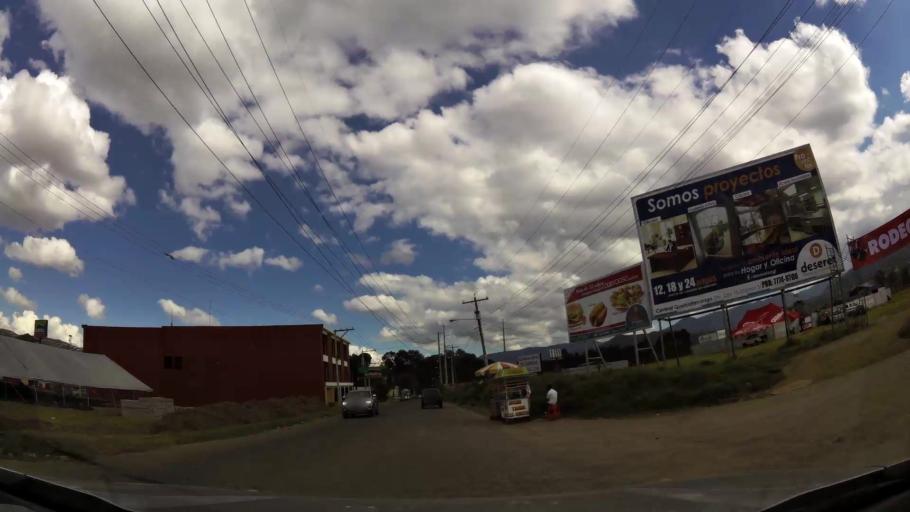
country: GT
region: Quetzaltenango
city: Quetzaltenango
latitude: 14.8468
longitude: -91.5392
